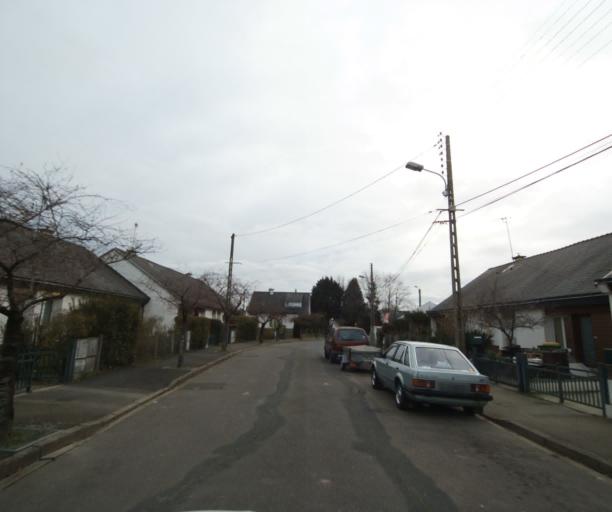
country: FR
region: Pays de la Loire
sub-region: Departement de la Sarthe
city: Le Mans
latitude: 47.9716
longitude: 0.2028
